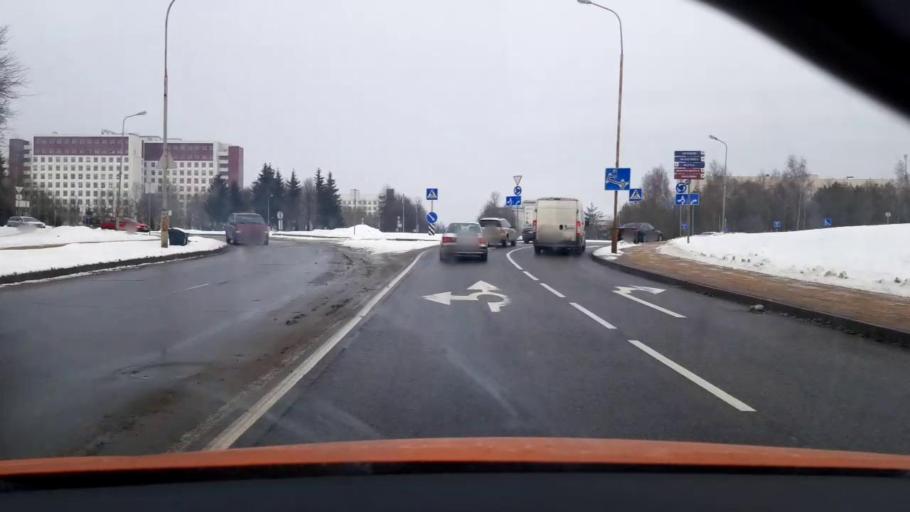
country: LT
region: Vilnius County
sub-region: Vilnius
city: Fabijoniskes
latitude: 54.7488
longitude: 25.2794
